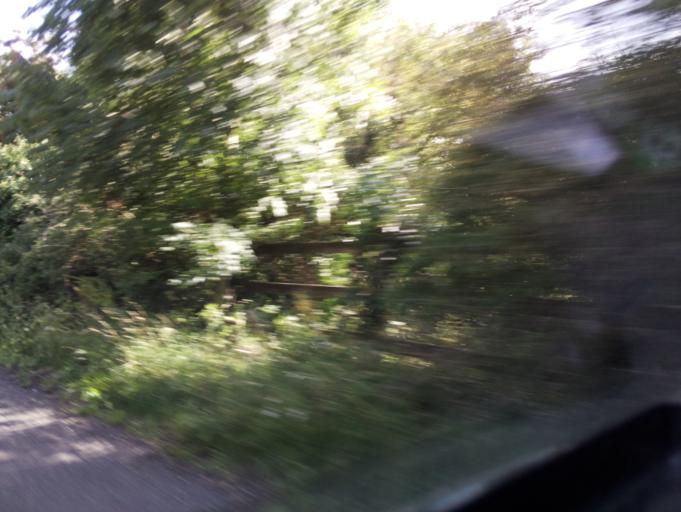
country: GB
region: England
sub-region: Gloucestershire
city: Cirencester
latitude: 51.7417
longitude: -1.9919
